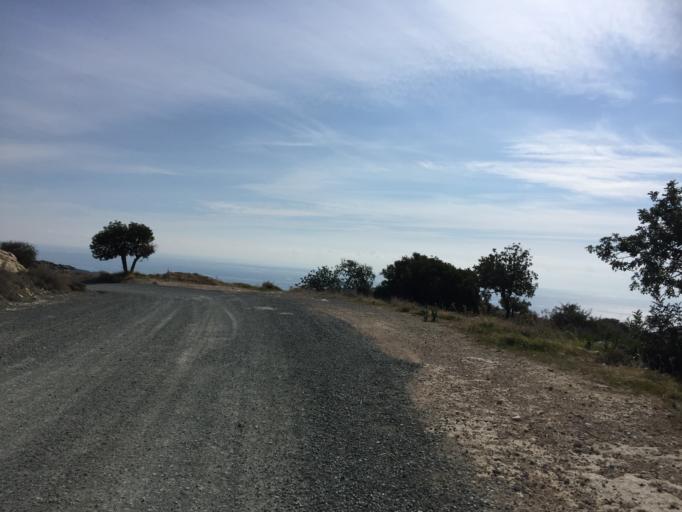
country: CY
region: Larnaka
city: Agios Tychon
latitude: 34.7411
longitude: 33.1232
